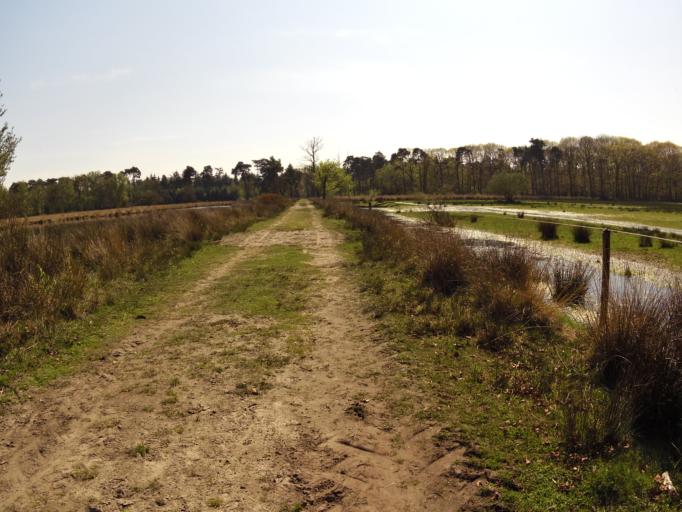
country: NL
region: North Brabant
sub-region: Gemeente Boxtel
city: Boxtel
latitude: 51.5727
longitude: 5.2836
